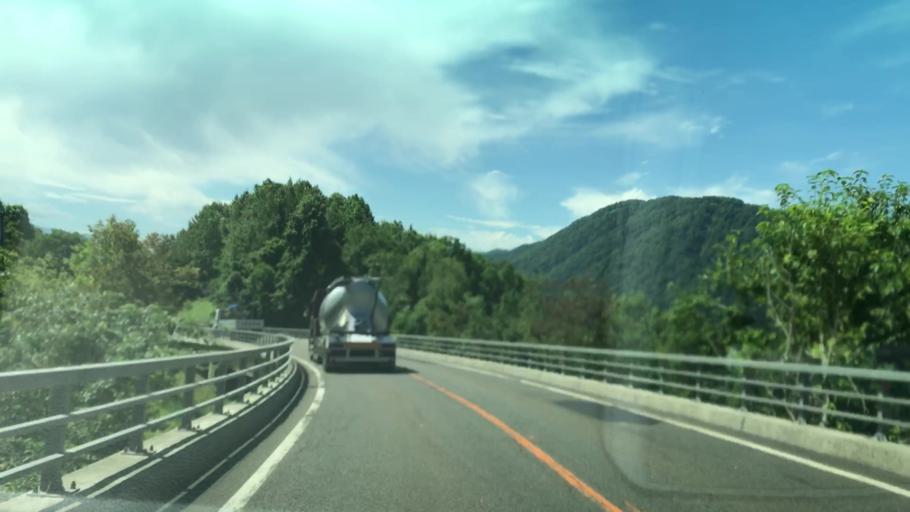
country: JP
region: Hokkaido
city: Shimo-furano
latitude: 42.8991
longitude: 142.4359
